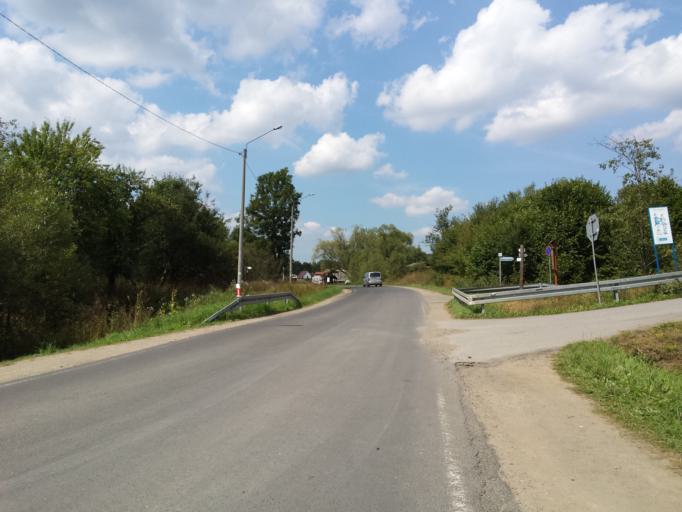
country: PL
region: Subcarpathian Voivodeship
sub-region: Powiat leski
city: Cisna
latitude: 49.1591
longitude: 22.4636
